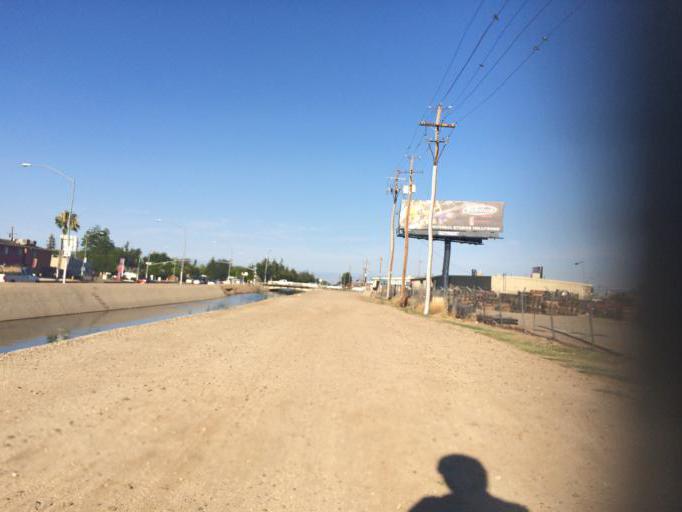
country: US
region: California
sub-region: Fresno County
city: Fresno
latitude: 36.7648
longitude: -119.7474
